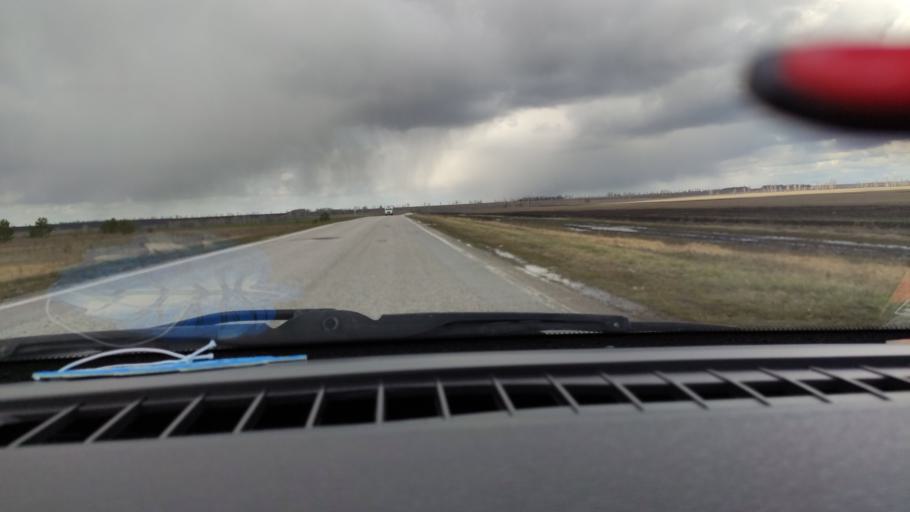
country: RU
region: Samara
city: Povolzhskiy
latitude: 53.7936
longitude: 49.7338
